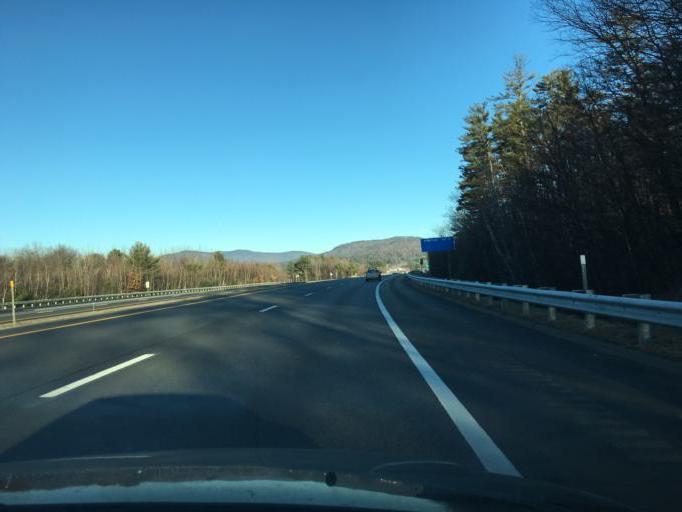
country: US
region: New Hampshire
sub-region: Grafton County
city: Plymouth
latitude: 43.7568
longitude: -71.6755
